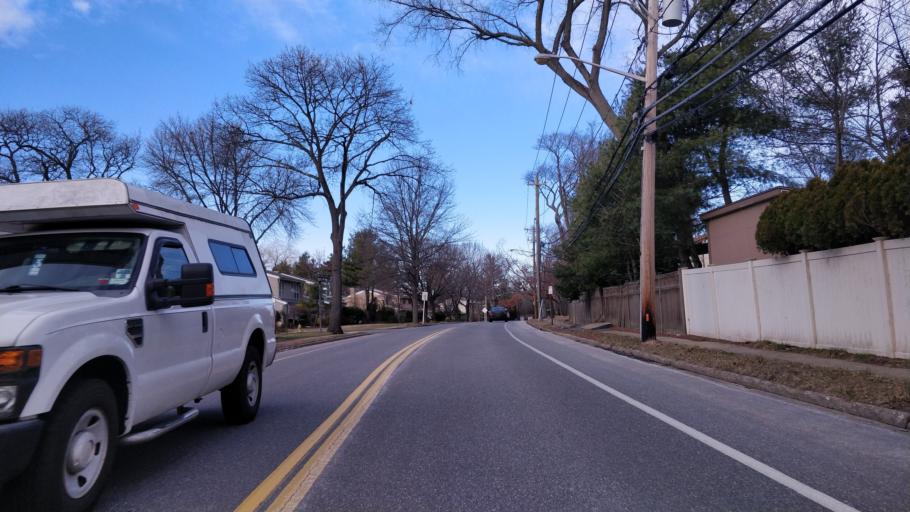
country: US
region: New York
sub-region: Suffolk County
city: Northport
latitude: 40.8922
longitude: -73.3438
